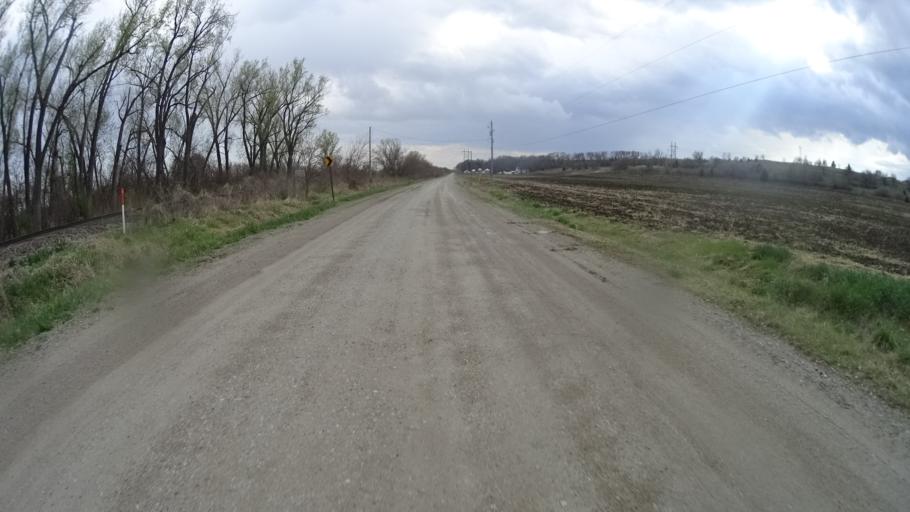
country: US
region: Nebraska
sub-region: Sarpy County
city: Offutt Air Force Base
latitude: 41.0928
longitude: -95.9139
